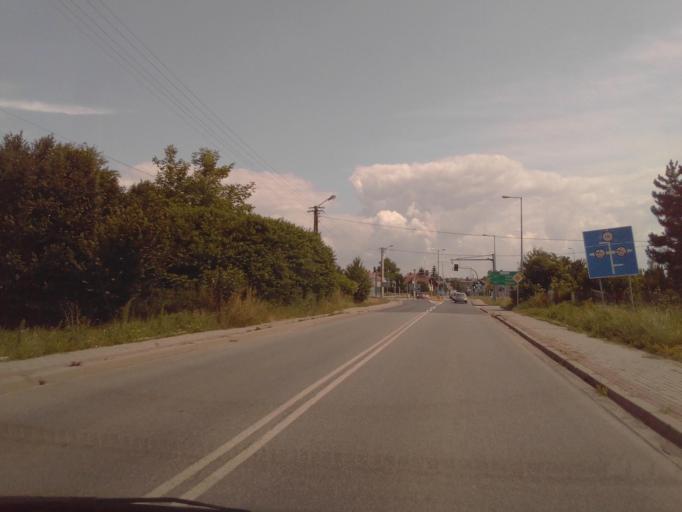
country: PL
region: Subcarpathian Voivodeship
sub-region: Powiat ropczycko-sedziszowski
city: Ropczyce
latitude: 50.0489
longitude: 21.6037
